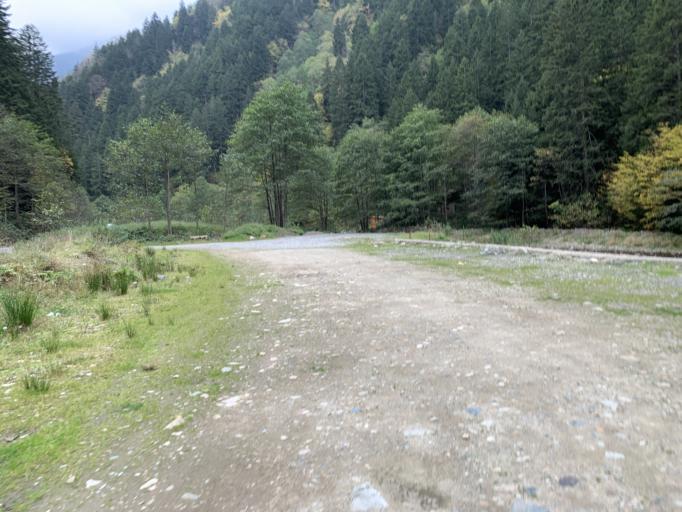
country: TR
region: Trabzon
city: Uzungol
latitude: 40.6015
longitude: 40.3167
